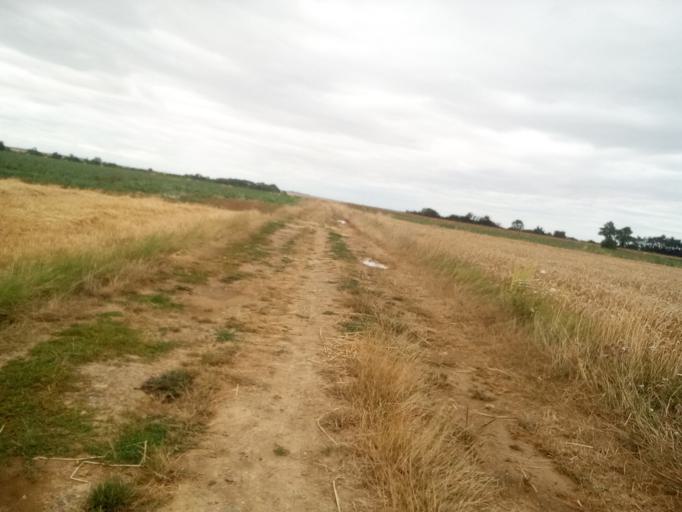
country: FR
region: Lower Normandy
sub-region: Departement du Calvados
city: Clinchamps-sur-Orne
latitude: 49.0571
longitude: -0.4115
